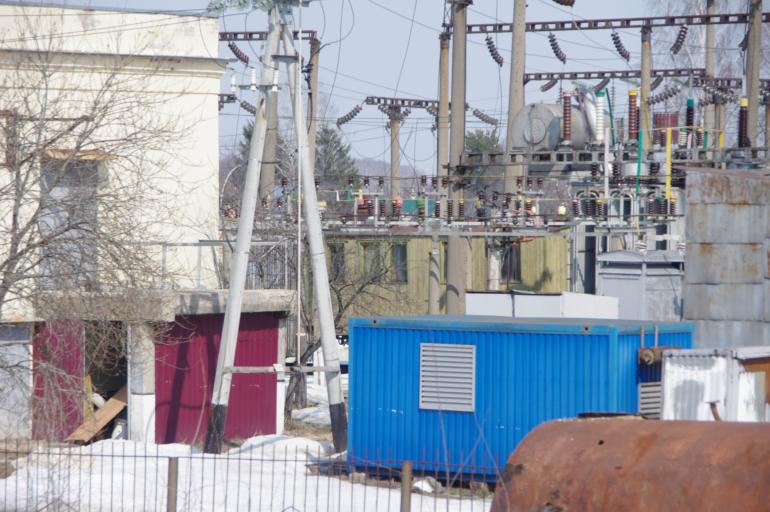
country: RU
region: Moskovskaya
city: Stolbovaya
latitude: 55.2352
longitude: 37.4924
